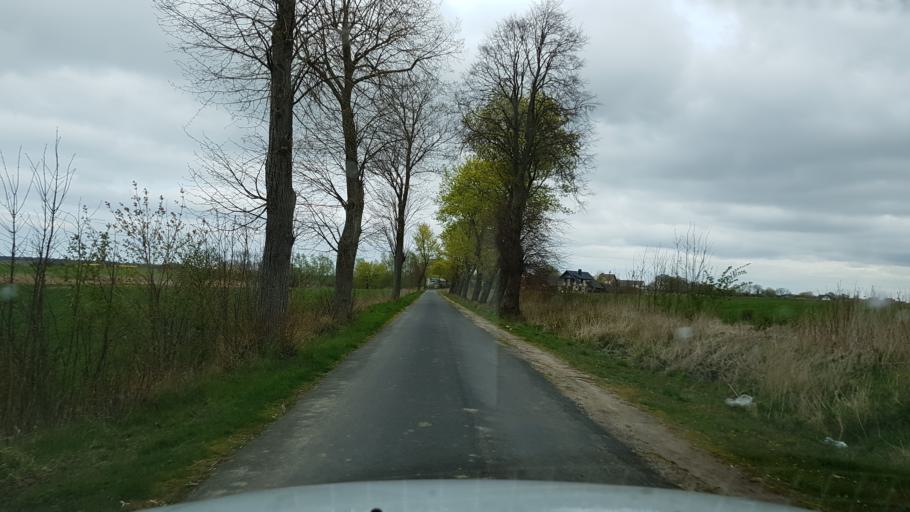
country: PL
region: West Pomeranian Voivodeship
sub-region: Powiat koszalinski
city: Mielno
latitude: 54.2292
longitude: 16.0415
